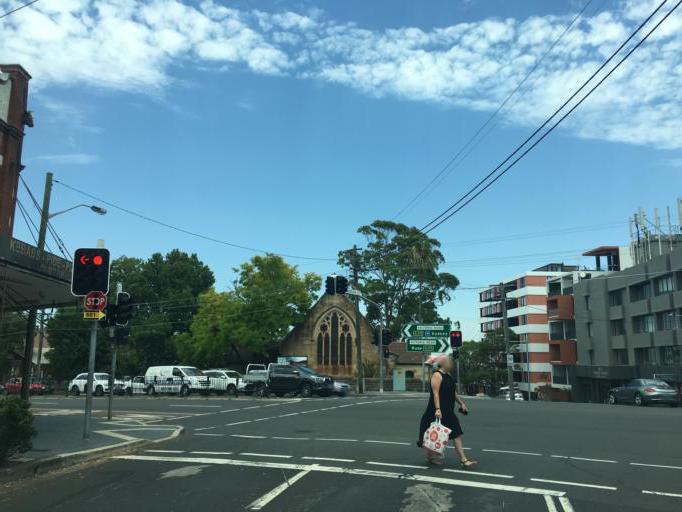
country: AU
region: New South Wales
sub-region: Hunters Hill
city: Gladesville
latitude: -33.8301
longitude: 151.1271
